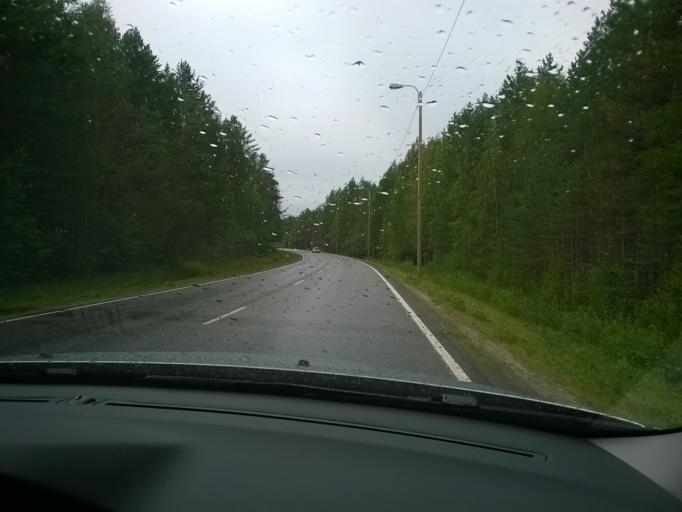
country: FI
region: Kainuu
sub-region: Kehys-Kainuu
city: Kuhmo
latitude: 64.1205
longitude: 29.5553
